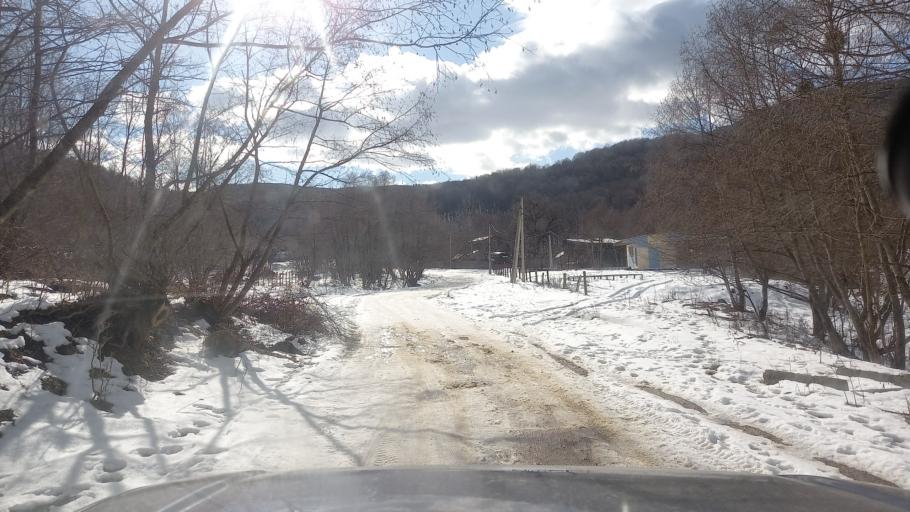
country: RU
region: Adygeya
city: Kamennomostskiy
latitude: 44.1952
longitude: 39.9607
